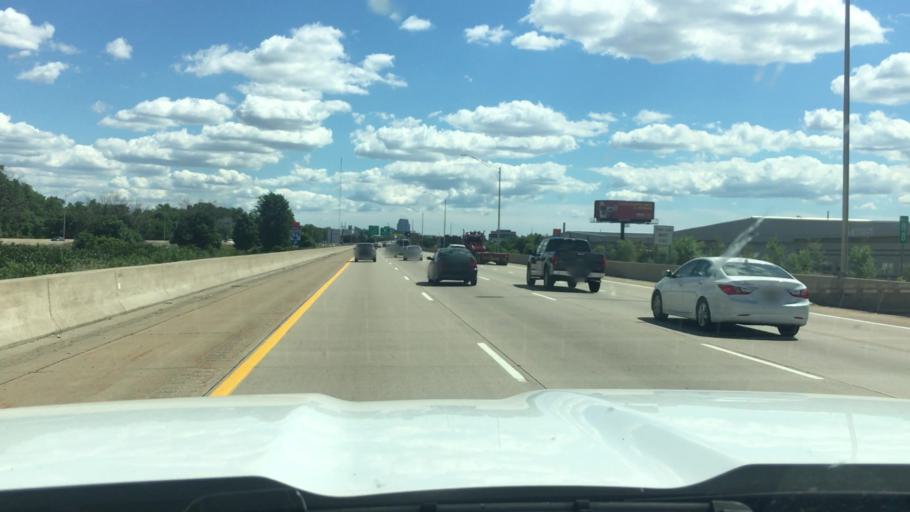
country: US
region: Michigan
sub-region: Kent County
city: Comstock Park
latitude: 43.0058
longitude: -85.6761
